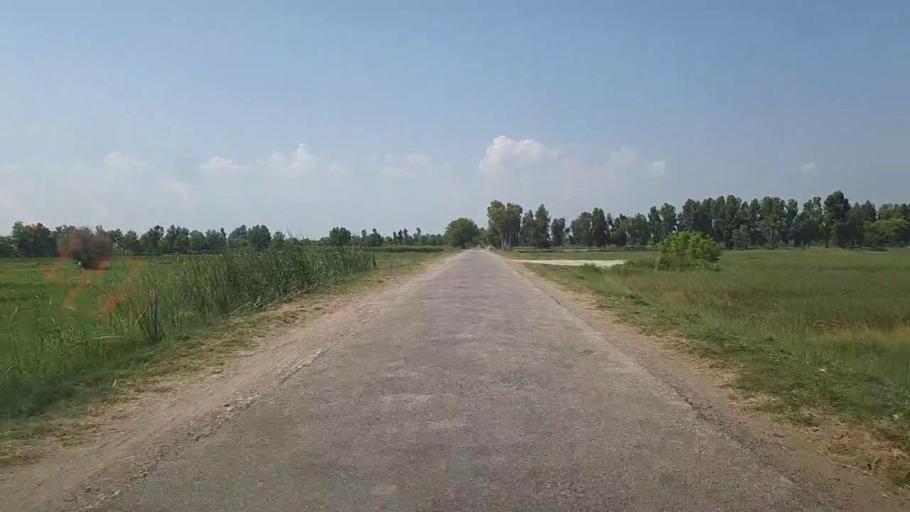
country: PK
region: Sindh
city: Khairpur
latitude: 28.0808
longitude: 69.6362
